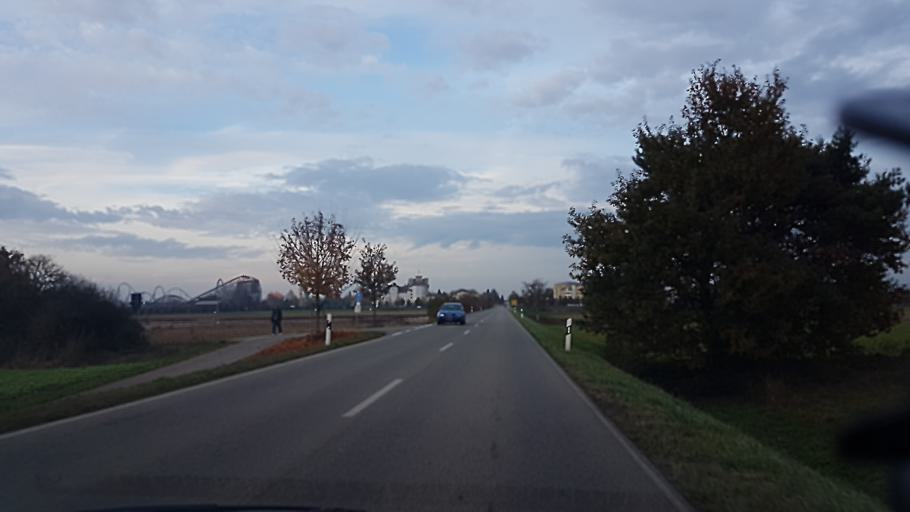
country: DE
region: Baden-Wuerttemberg
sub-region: Freiburg Region
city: Rust
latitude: 48.2545
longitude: 7.7187
